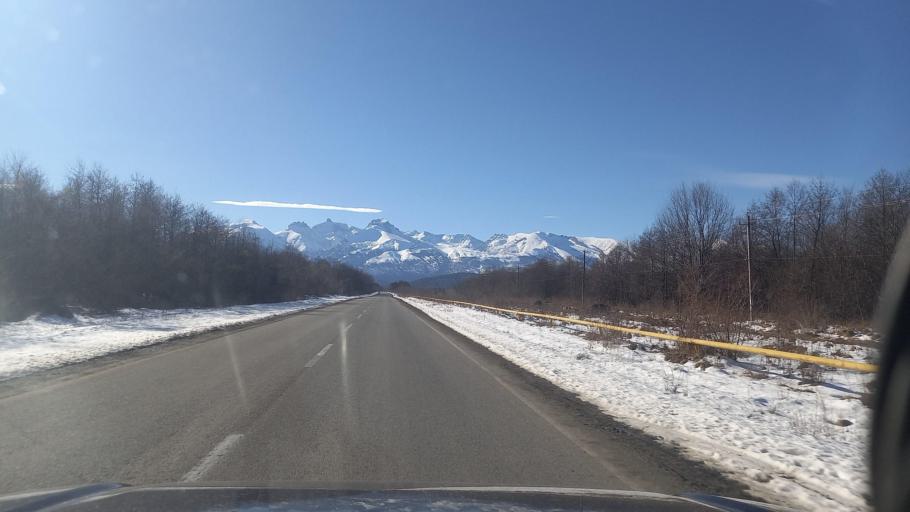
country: RU
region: North Ossetia
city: Chikola
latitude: 43.1614
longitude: 43.8518
